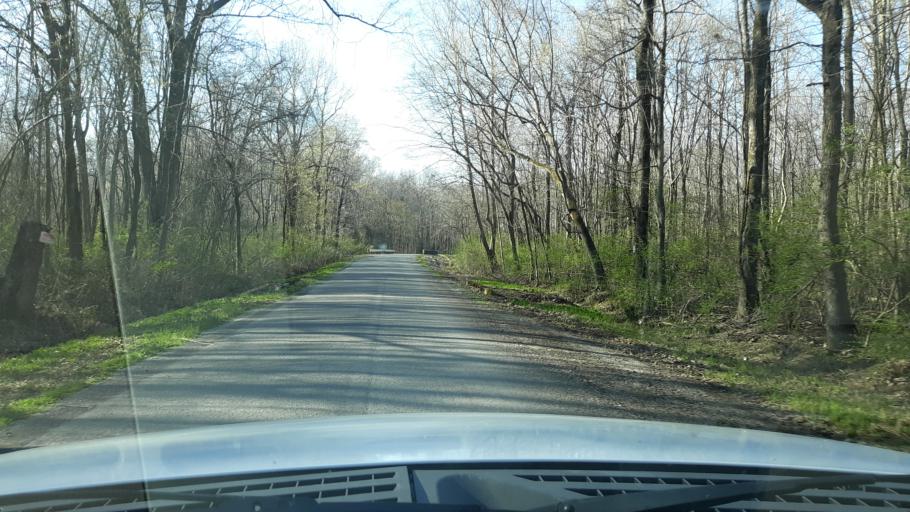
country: US
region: Illinois
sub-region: Saline County
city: Harrisburg
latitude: 37.7584
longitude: -88.5686
